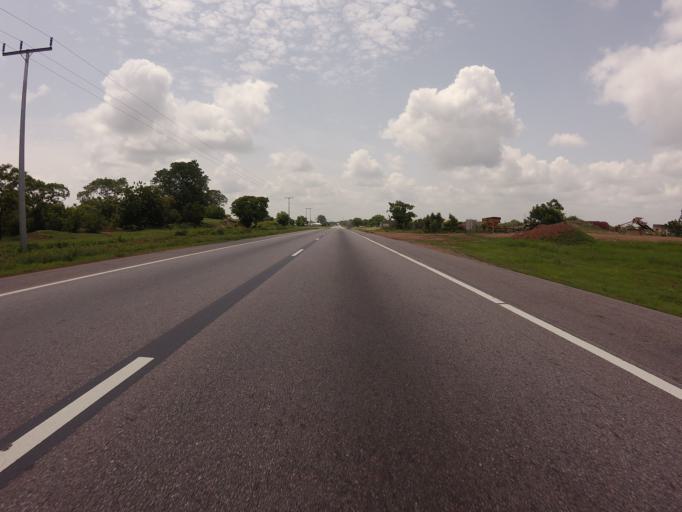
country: GH
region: Northern
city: Tamale
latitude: 9.1296
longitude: -1.2102
